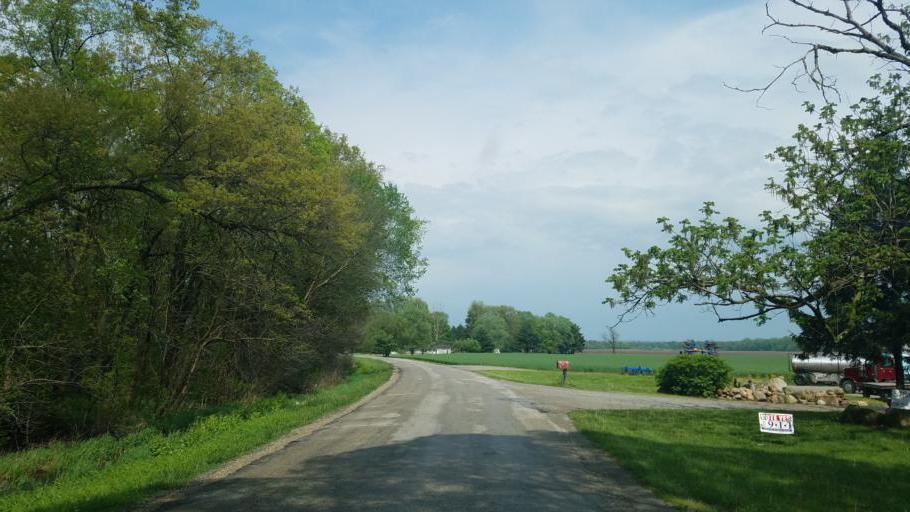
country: US
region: Ohio
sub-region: Licking County
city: Hebron
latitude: 39.9477
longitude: -82.5069
